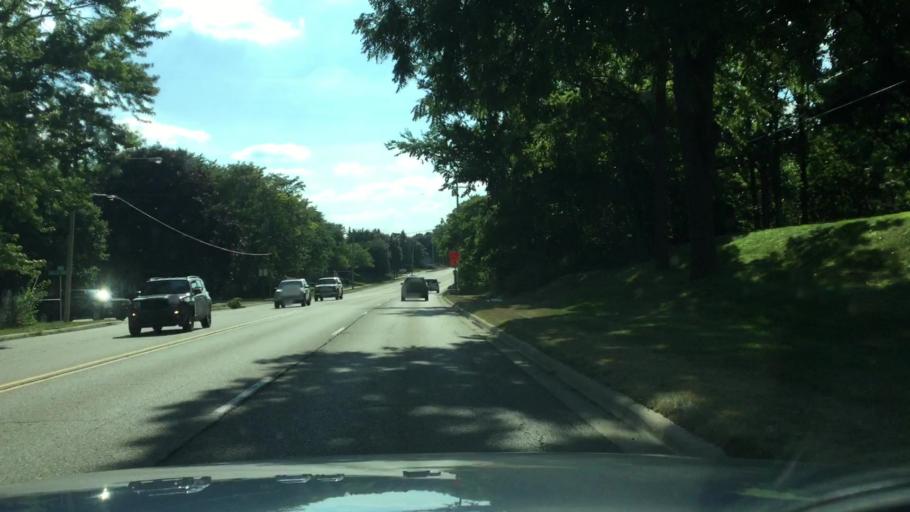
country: US
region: Michigan
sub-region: Genesee County
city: Grand Blanc
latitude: 42.9253
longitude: -83.6159
